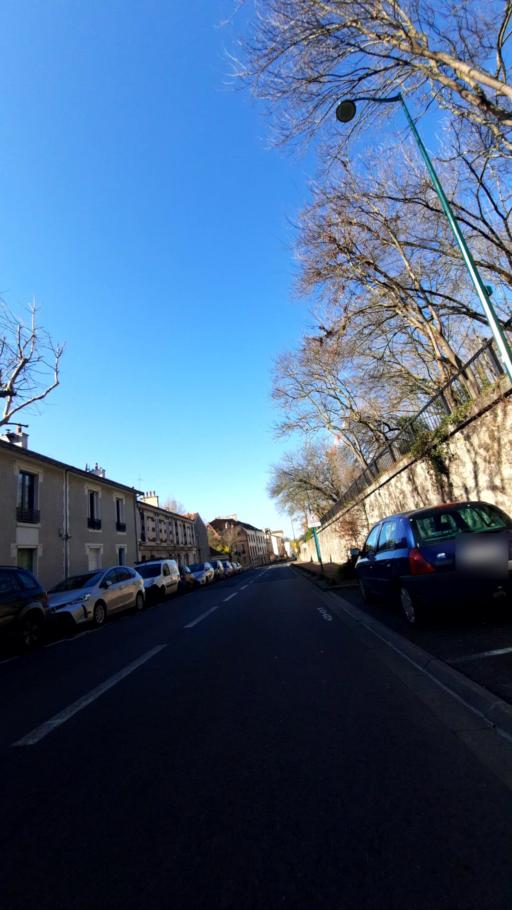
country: FR
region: Ile-de-France
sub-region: Departement du Val-de-Marne
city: Maisons-Alfort
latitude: 48.8183
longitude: 2.4386
